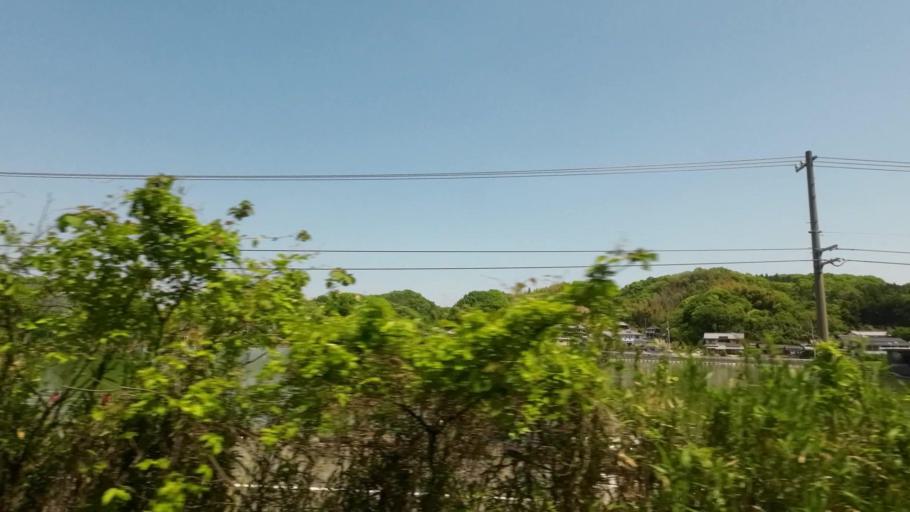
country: JP
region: Ehime
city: Hojo
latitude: 34.0957
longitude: 132.9386
